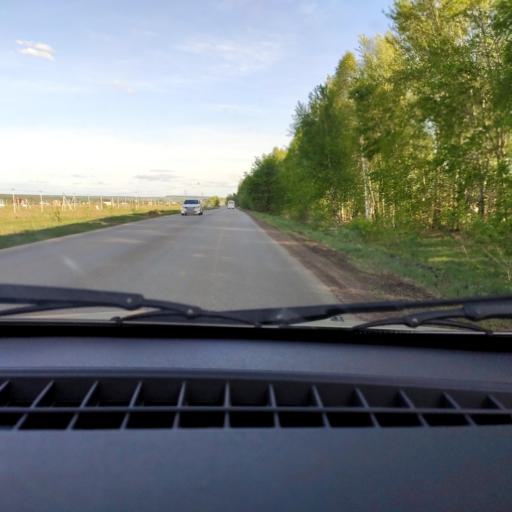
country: RU
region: Bashkortostan
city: Kabakovo
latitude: 54.6768
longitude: 56.1380
